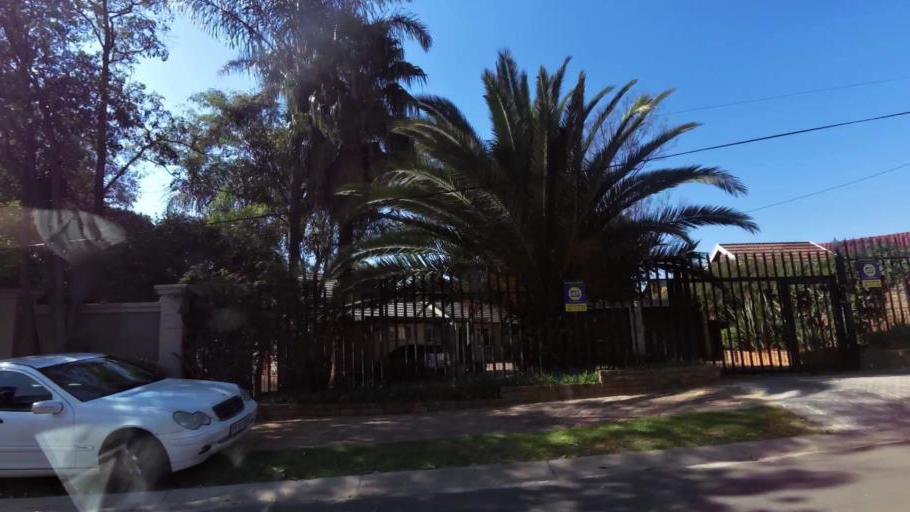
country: ZA
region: Gauteng
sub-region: City of Johannesburg Metropolitan Municipality
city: Roodepoort
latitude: -26.1503
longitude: 27.9446
